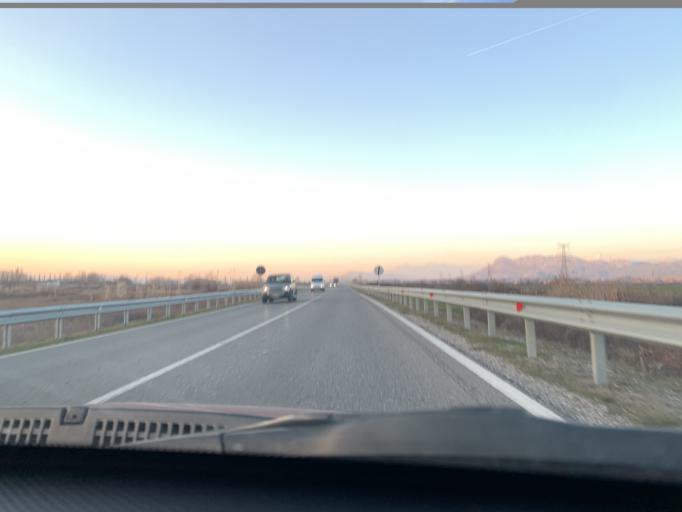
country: AL
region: Lezhe
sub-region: Rrethi i Lezhes
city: Balldreni i Ri
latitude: 41.8427
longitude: 19.6438
